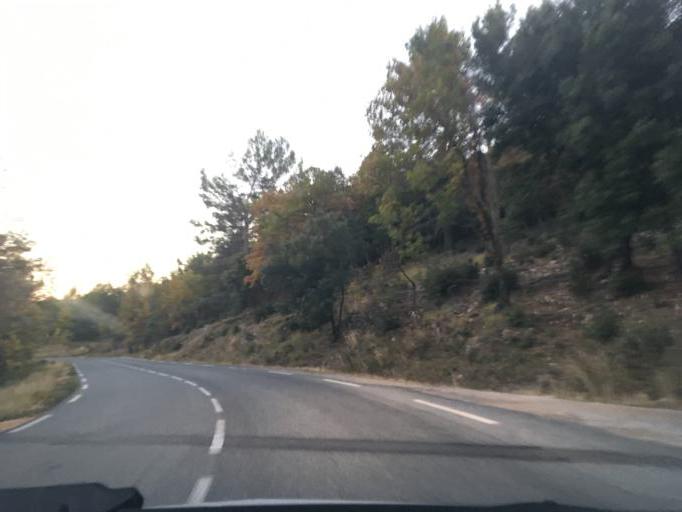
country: FR
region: Provence-Alpes-Cote d'Azur
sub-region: Departement du Var
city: Montferrat
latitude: 43.6323
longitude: 6.4877
